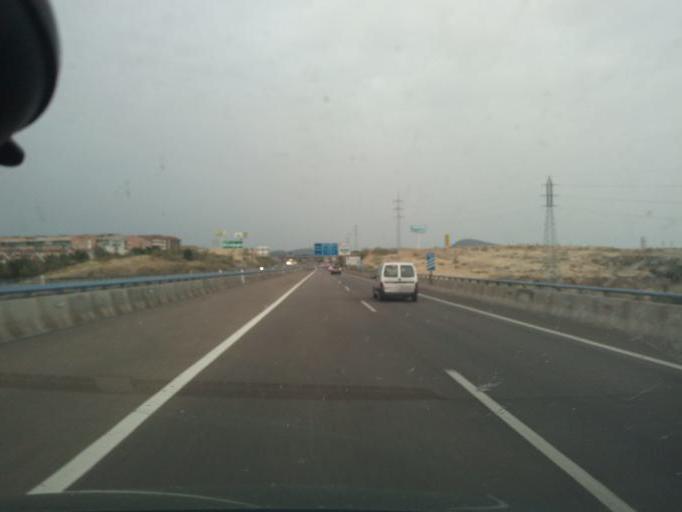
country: ES
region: Extremadura
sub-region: Provincia de Badajoz
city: Merida
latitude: 38.9276
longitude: -6.3692
